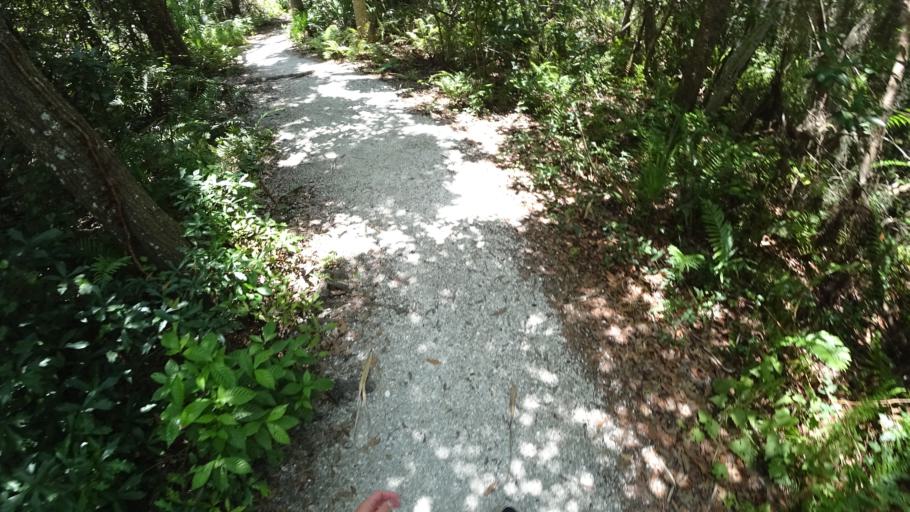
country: US
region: Florida
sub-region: Manatee County
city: West Bradenton
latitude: 27.5208
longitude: -82.6405
